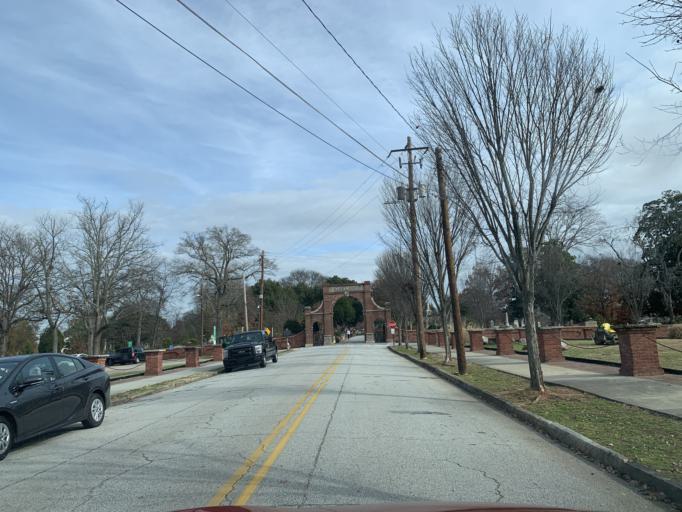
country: US
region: Georgia
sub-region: Fulton County
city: Atlanta
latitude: 33.7474
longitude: -84.3759
